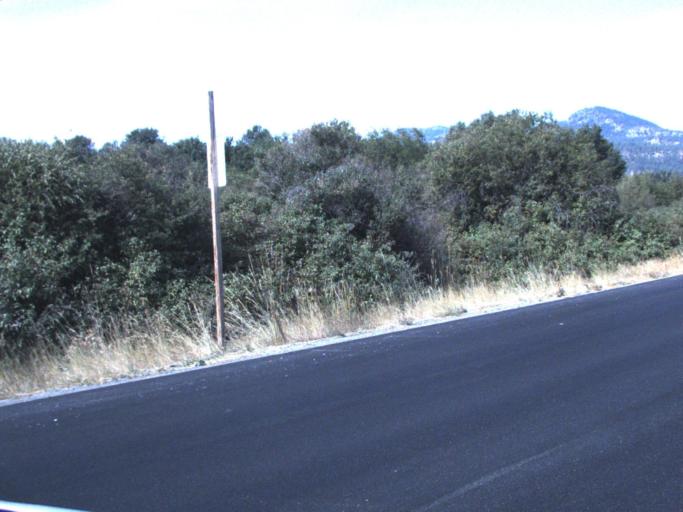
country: US
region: Washington
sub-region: Stevens County
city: Colville
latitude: 48.4714
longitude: -117.8906
